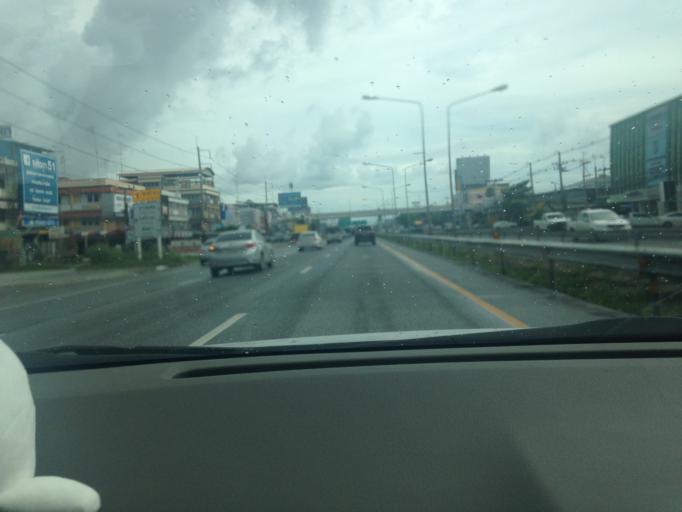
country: TH
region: Chon Buri
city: Chon Buri
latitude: 13.2997
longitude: 100.9479
